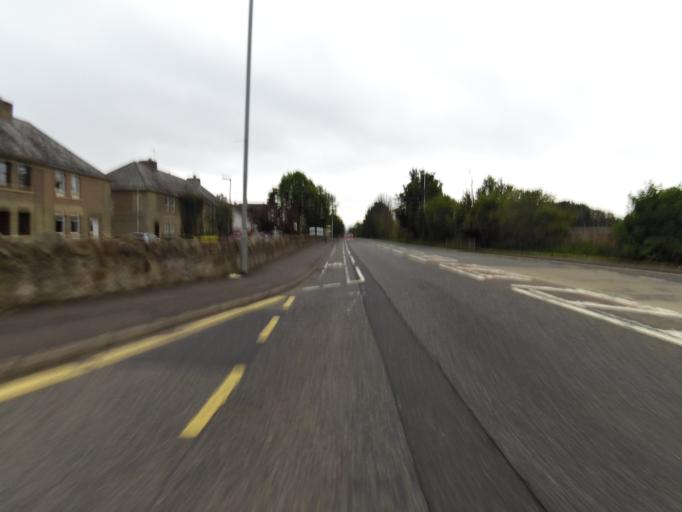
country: GB
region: Scotland
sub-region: Midlothian
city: Bonnyrigg
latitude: 55.9105
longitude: -3.1100
